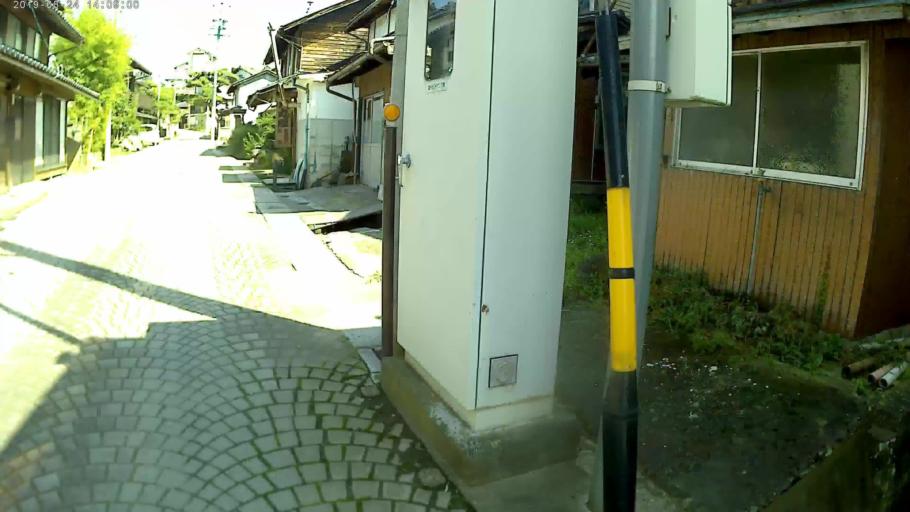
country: JP
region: Nagano
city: Komoro
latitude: 36.2710
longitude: 138.4189
